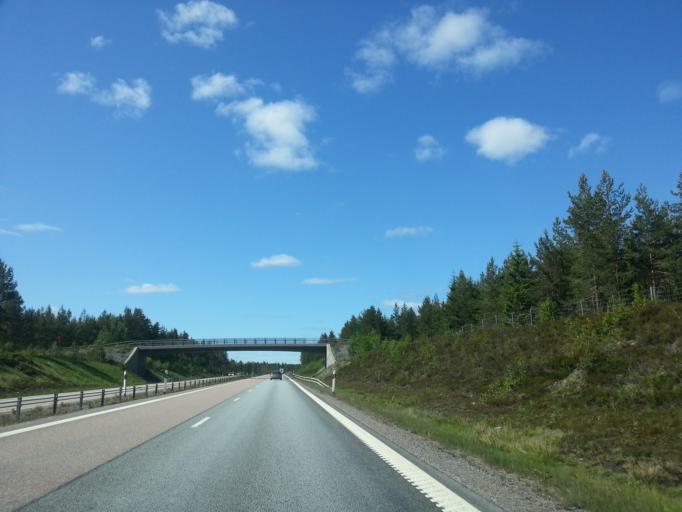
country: SE
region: Gaevleborg
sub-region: Soderhamns Kommun
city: Soderhamn
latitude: 61.3712
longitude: 17.0046
